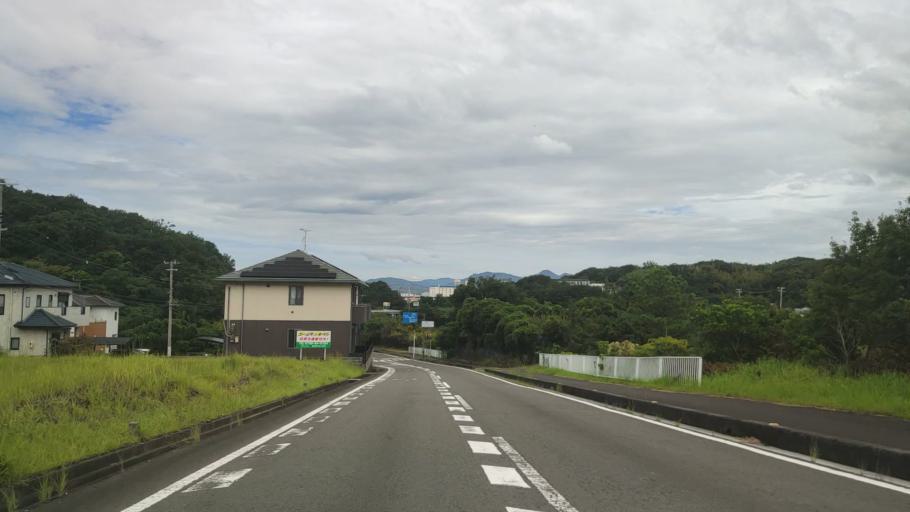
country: JP
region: Wakayama
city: Tanabe
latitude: 33.6896
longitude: 135.3881
